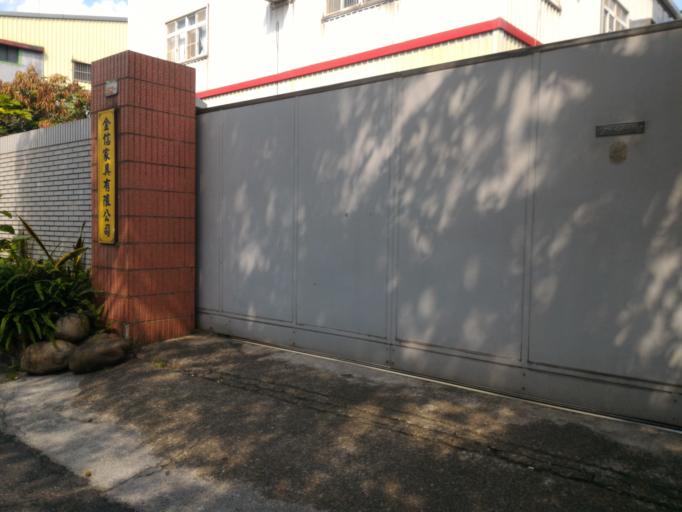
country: TW
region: Taipei
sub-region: Taipei
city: Banqiao
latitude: 24.9626
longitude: 121.4006
